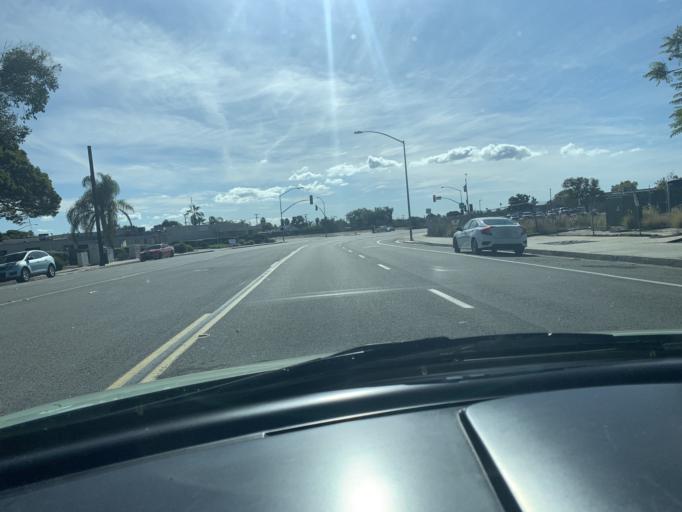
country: US
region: California
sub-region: San Diego County
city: San Diego
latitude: 32.8029
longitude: -117.1288
